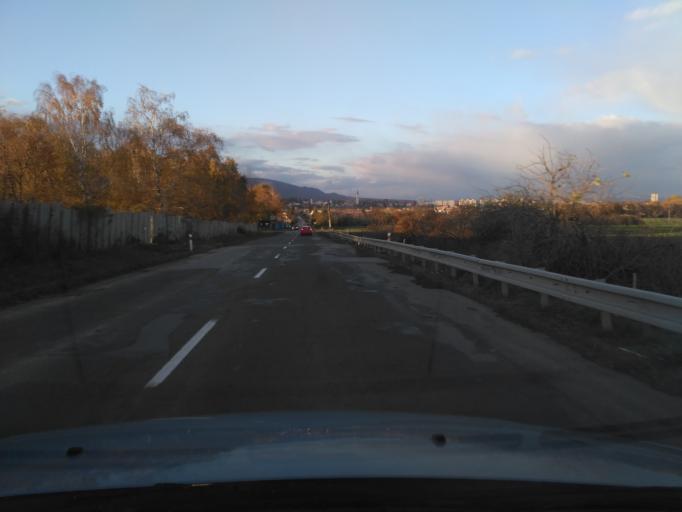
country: SK
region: Kosicky
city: Secovce
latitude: 48.6864
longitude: 21.6549
